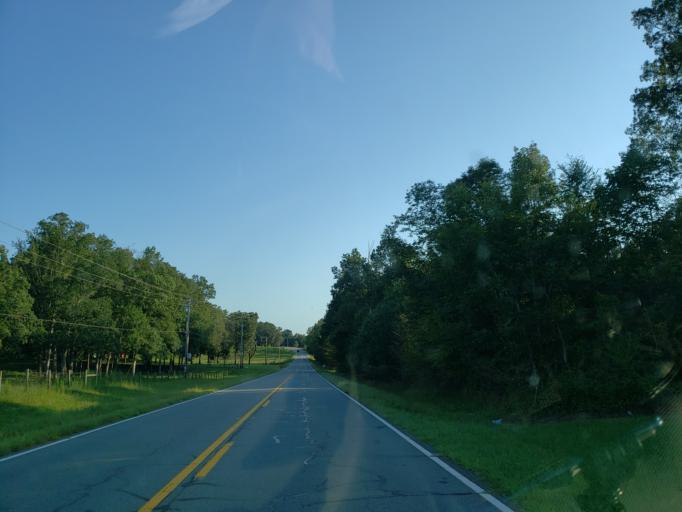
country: US
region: Georgia
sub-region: Murray County
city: Chatsworth
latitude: 34.7114
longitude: -84.8193
